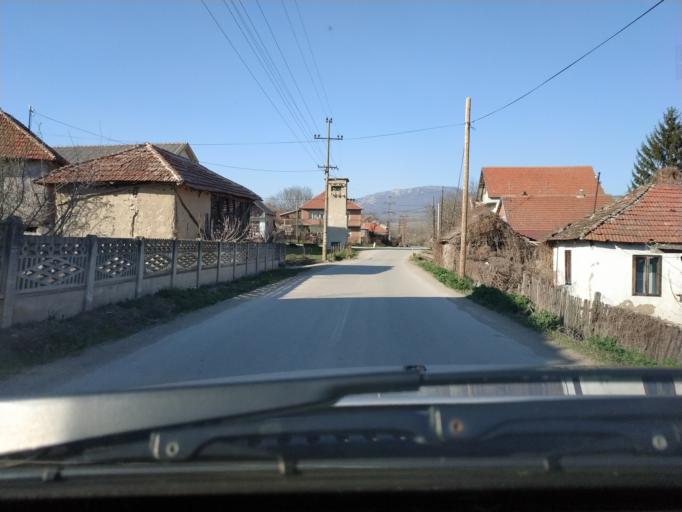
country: RS
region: Central Serbia
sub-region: Nisavski Okrug
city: Aleksinac
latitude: 43.5100
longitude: 21.7976
